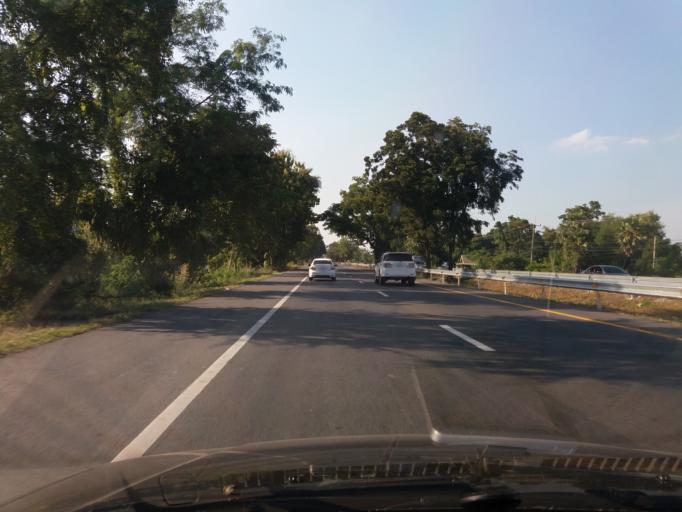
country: TH
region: Nakhon Sawan
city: Kao Liao
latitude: 15.7987
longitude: 99.9585
